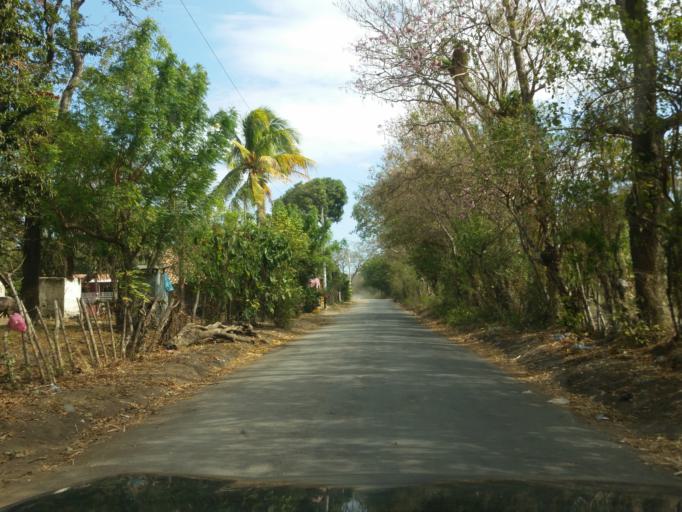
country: NI
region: Rivas
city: Potosi
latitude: 11.4929
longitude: -85.8594
